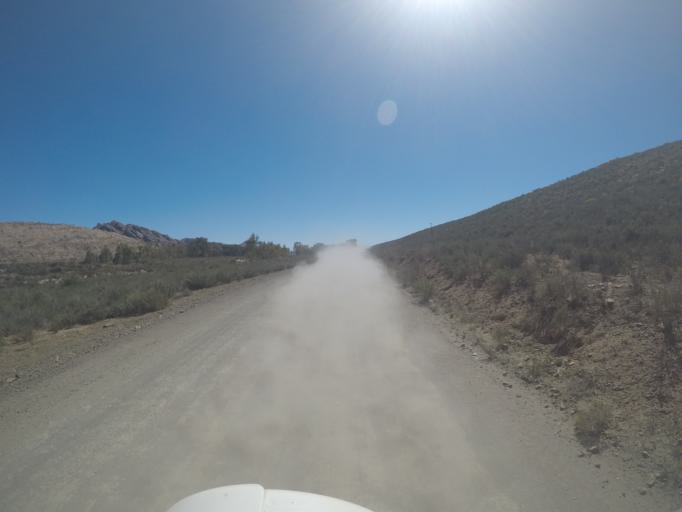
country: ZA
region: Western Cape
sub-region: Cape Winelands District Municipality
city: Ceres
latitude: -32.8168
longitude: 19.4519
